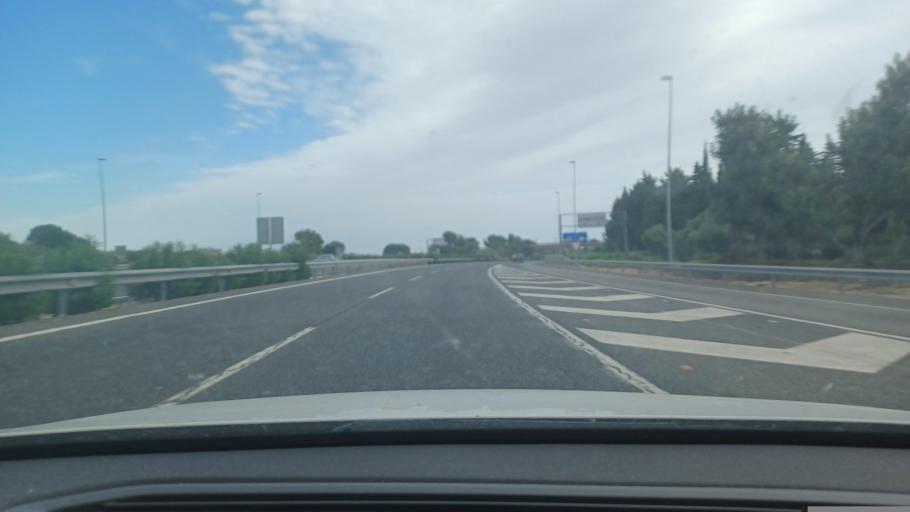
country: ES
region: Catalonia
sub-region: Provincia de Tarragona
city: Vila-seca
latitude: 41.1048
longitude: 1.1356
